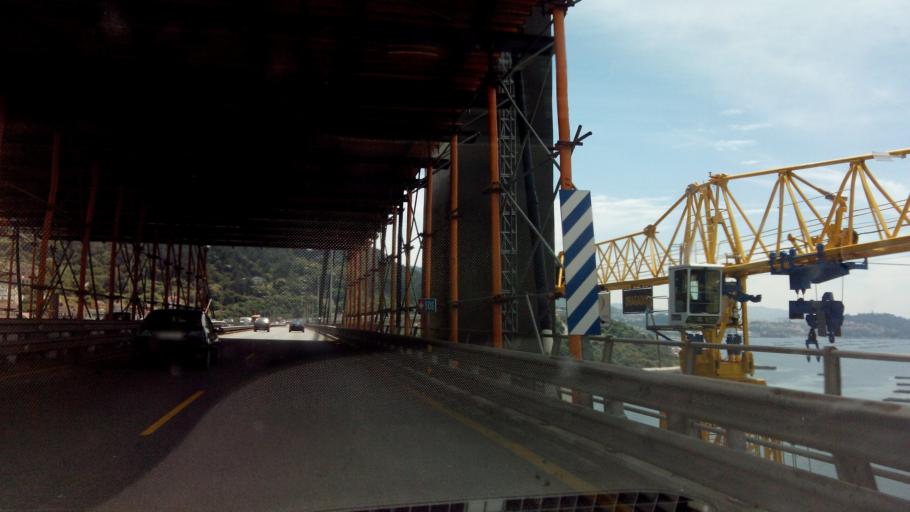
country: ES
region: Galicia
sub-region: Provincia de Pontevedra
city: Redondela
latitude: 42.2869
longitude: -8.6607
